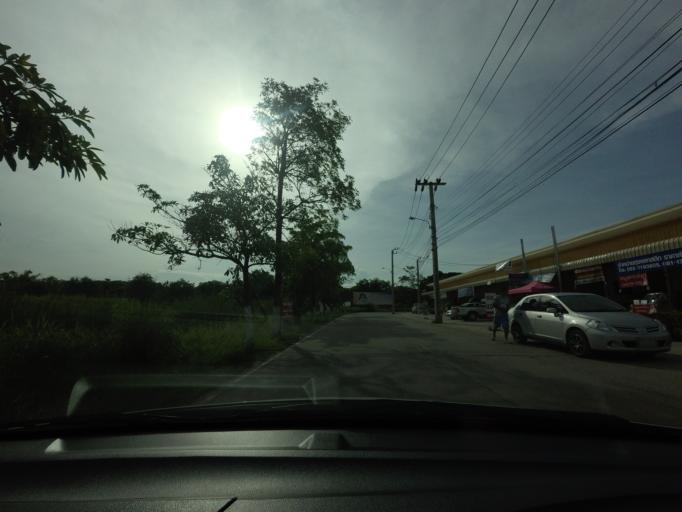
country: TH
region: Bangkok
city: Bang Na
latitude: 13.6406
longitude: 100.6608
